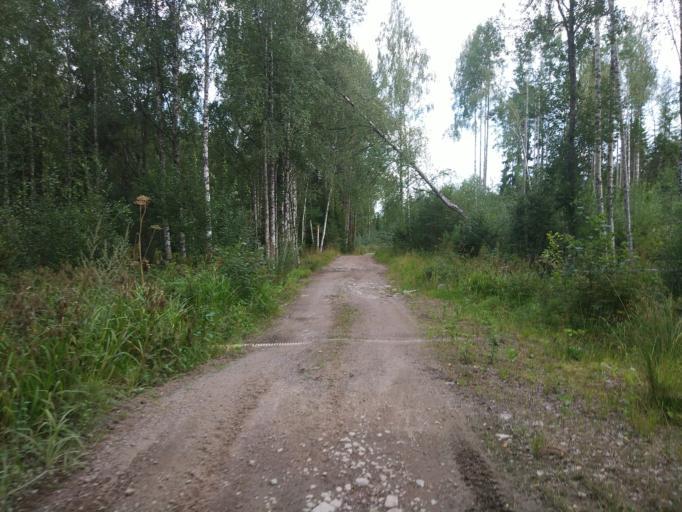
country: RU
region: Leningrad
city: Kuznechnoye
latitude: 61.1113
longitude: 29.6120
